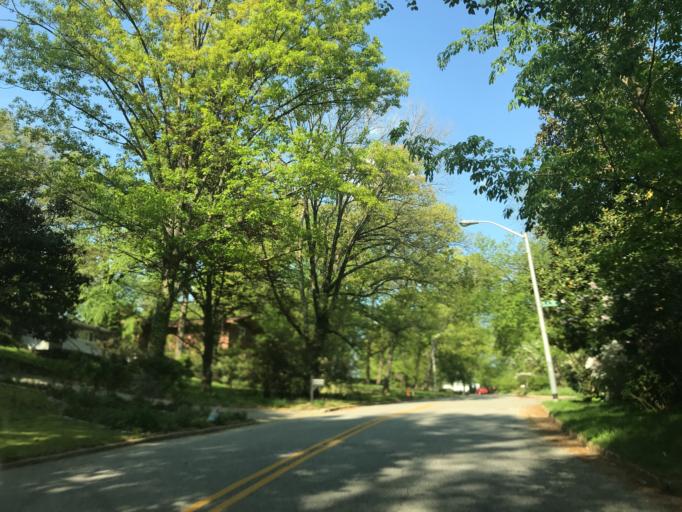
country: US
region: Maryland
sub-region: Baltimore County
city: Pikesville
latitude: 39.3699
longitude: -76.6657
